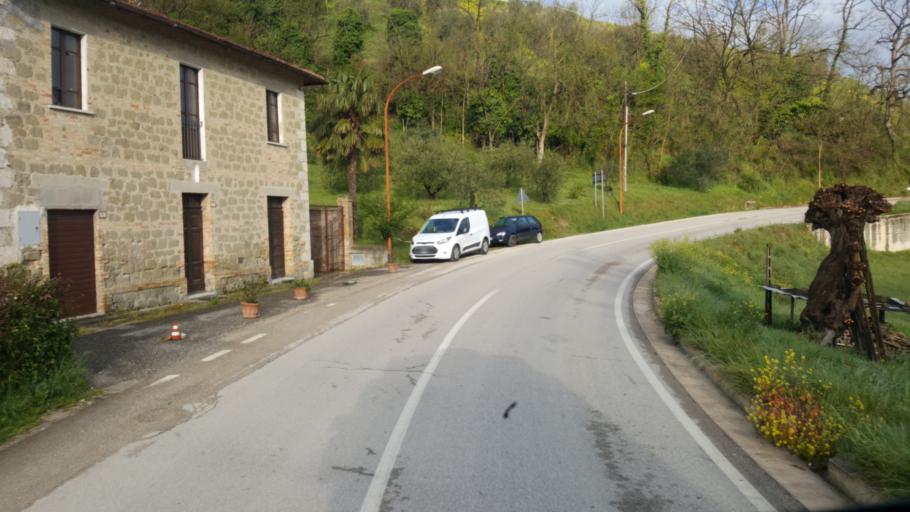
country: IT
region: The Marches
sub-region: Provincia di Ascoli Piceno
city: Venarotta
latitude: 42.8703
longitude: 13.5344
